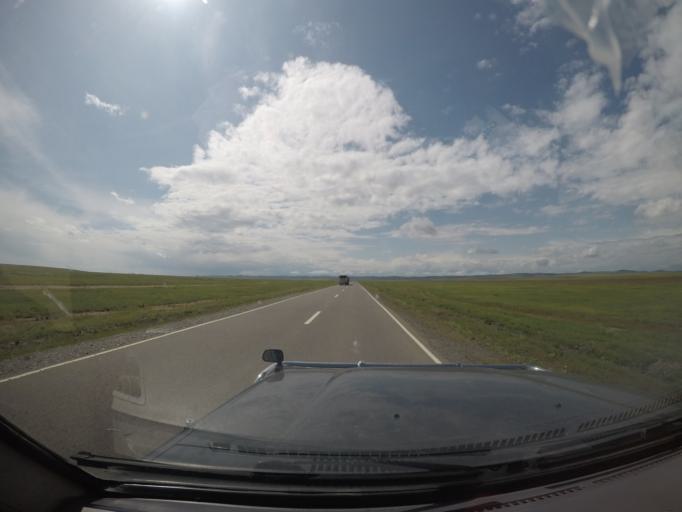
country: MN
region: Hentiy
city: Moron
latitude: 47.4197
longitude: 109.9976
